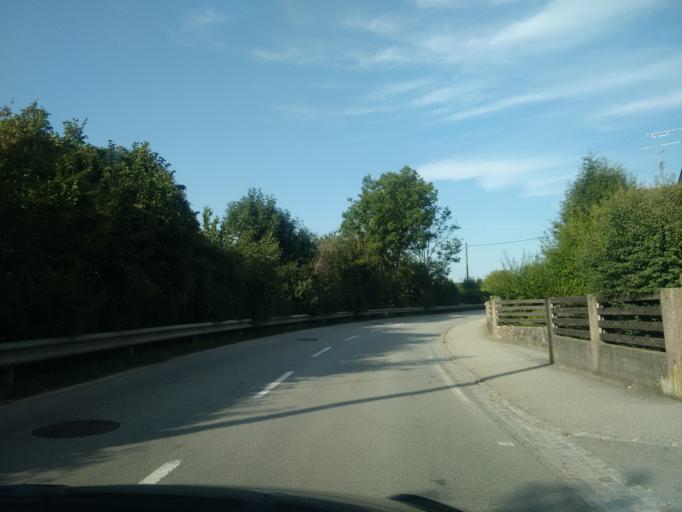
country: DE
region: Bavaria
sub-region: Lower Bavaria
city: Kirchdorf am Inn
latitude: 48.2308
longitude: 13.0091
